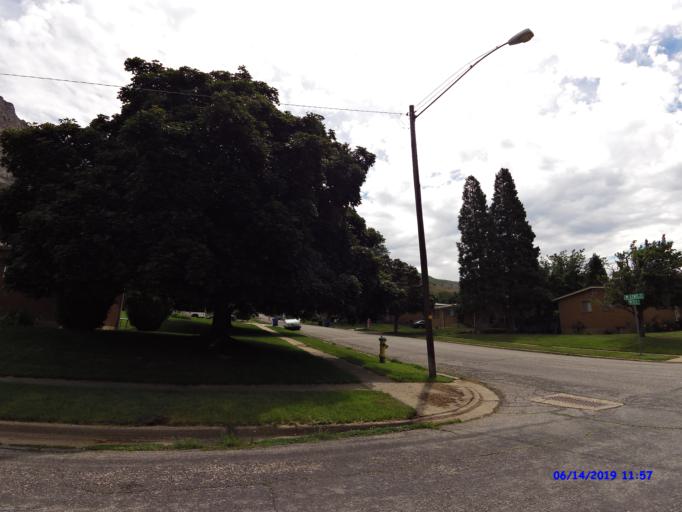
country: US
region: Utah
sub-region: Weber County
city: Ogden
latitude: 41.2584
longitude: -111.9449
